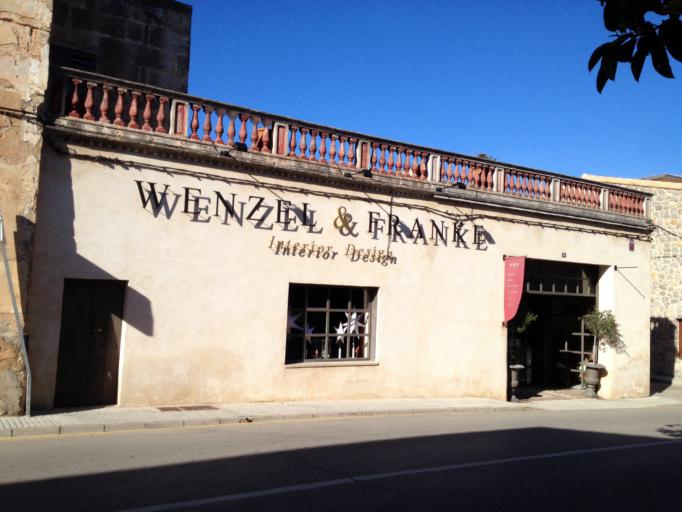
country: ES
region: Balearic Islands
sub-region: Illes Balears
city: Sant Llorenc des Cardassar
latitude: 39.6123
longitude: 3.2851
